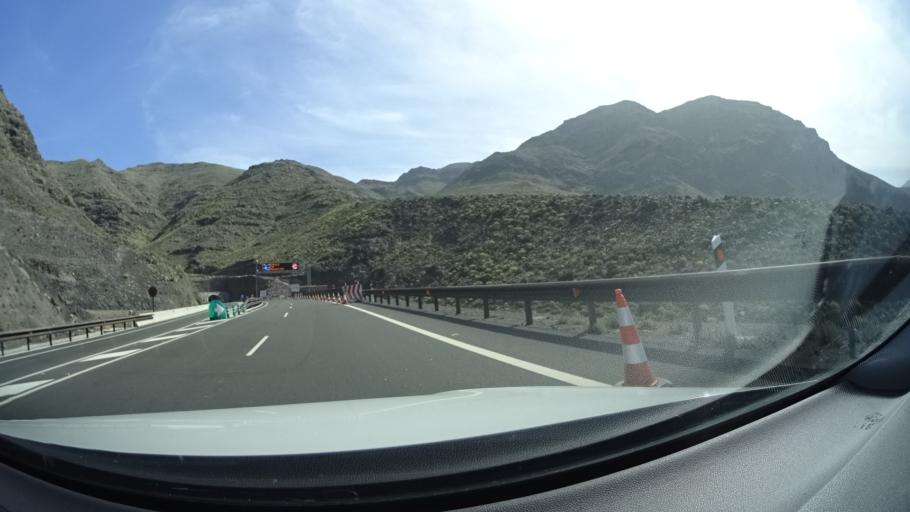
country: ES
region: Canary Islands
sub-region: Provincia de Las Palmas
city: San Nicolas
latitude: 28.0206
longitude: -15.7658
